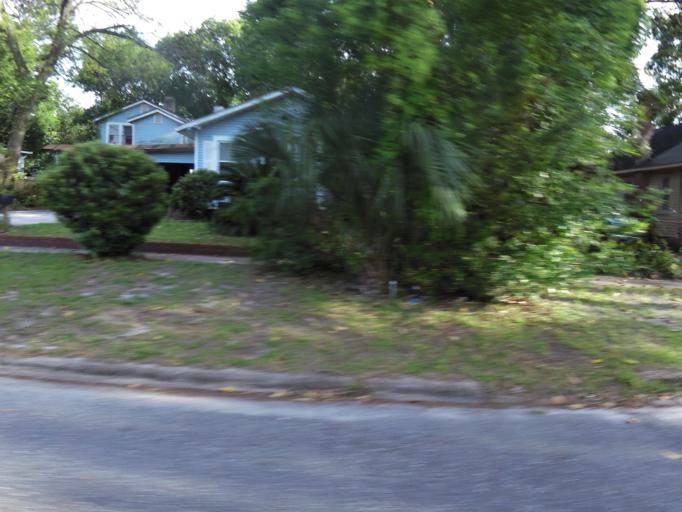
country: US
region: Florida
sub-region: Duval County
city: Jacksonville
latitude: 30.3704
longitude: -81.6542
